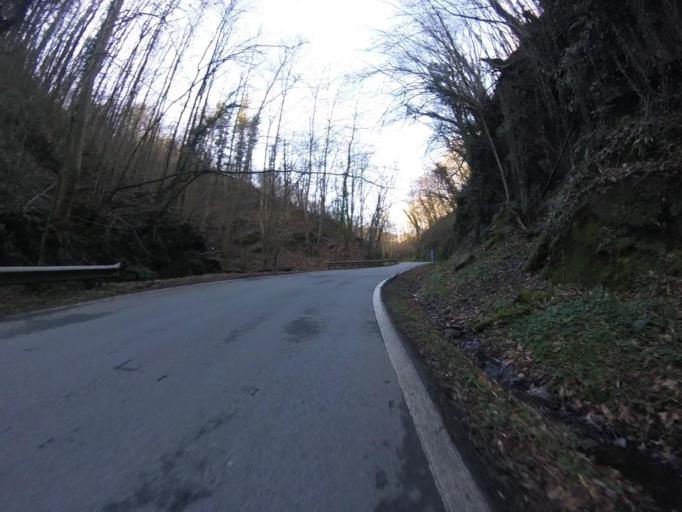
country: ES
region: Navarre
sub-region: Provincia de Navarra
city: Lesaka
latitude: 43.2518
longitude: -1.7219
